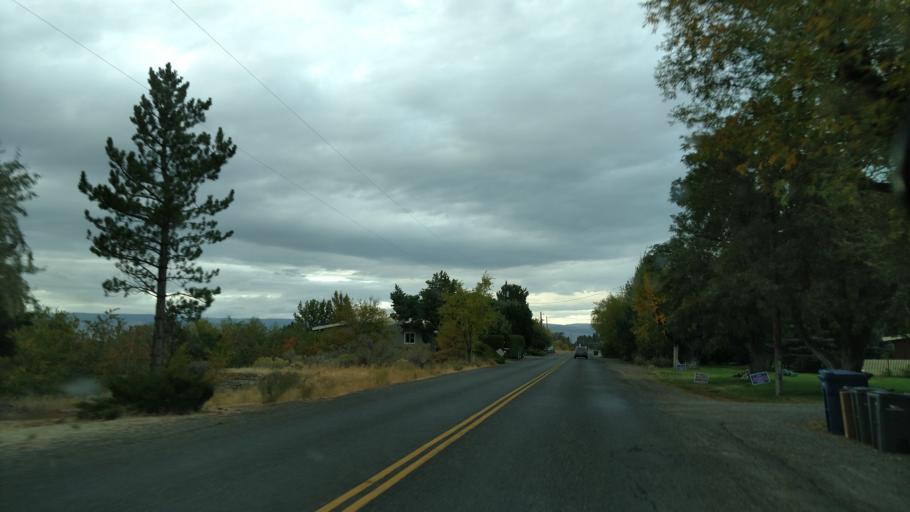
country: US
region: Washington
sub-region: Kittitas County
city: Ellensburg
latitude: 47.0075
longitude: -120.5250
